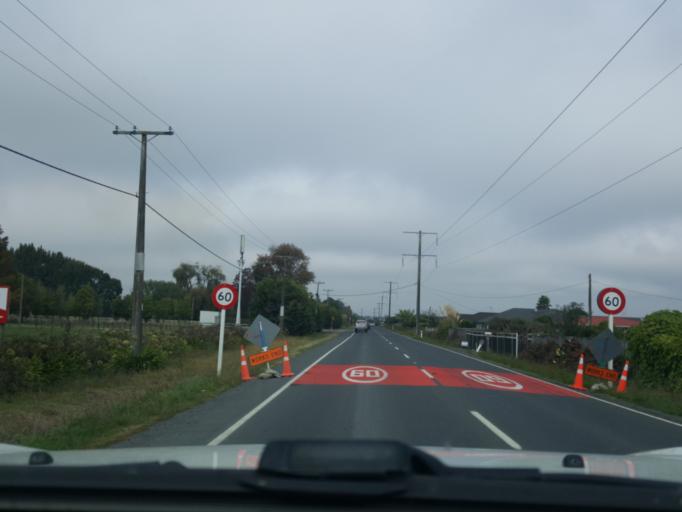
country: NZ
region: Waikato
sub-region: Hamilton City
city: Hamilton
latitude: -37.7354
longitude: 175.2880
